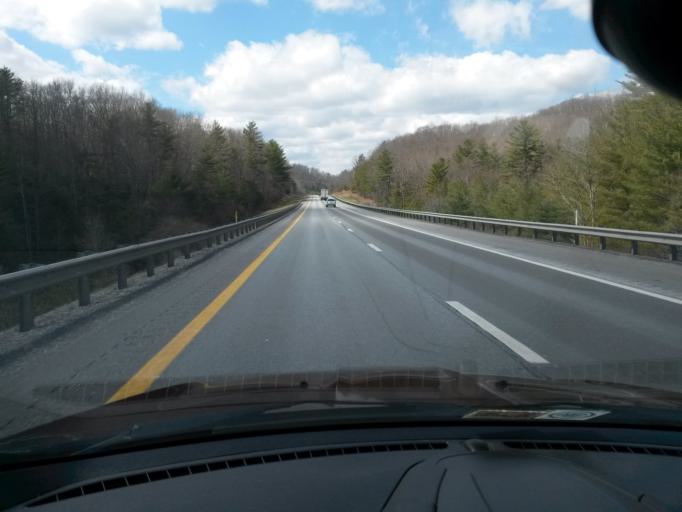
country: US
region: West Virginia
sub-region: Raleigh County
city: Shady Spring
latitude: 37.7028
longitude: -81.1425
